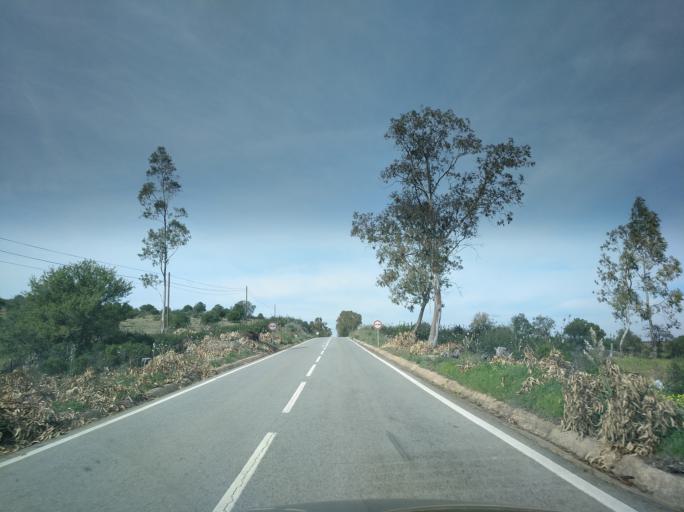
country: PT
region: Beja
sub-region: Mertola
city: Mertola
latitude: 37.5742
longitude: -7.6819
